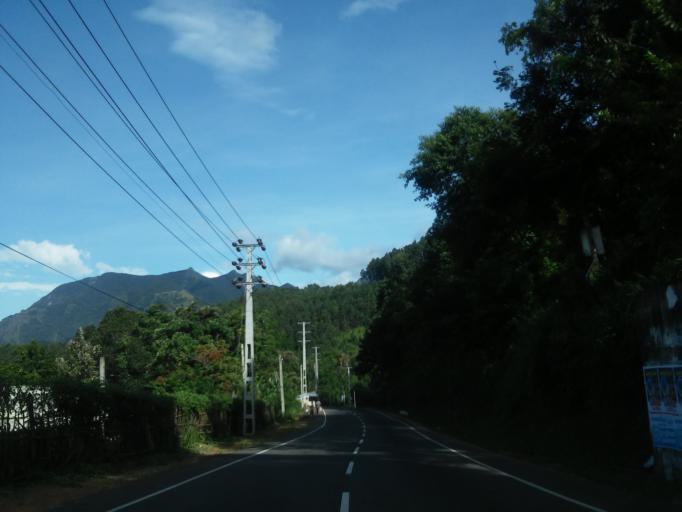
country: LK
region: Uva
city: Haputale
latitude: 6.7646
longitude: 80.8693
